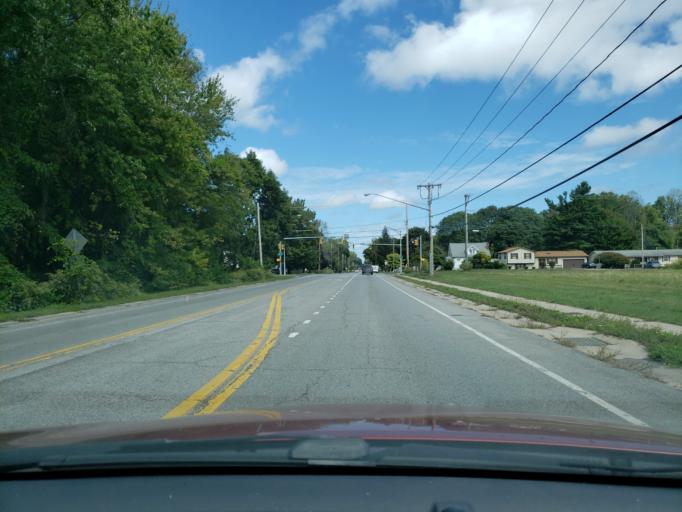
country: US
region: New York
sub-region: Monroe County
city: Greece
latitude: 43.2307
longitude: -77.7336
